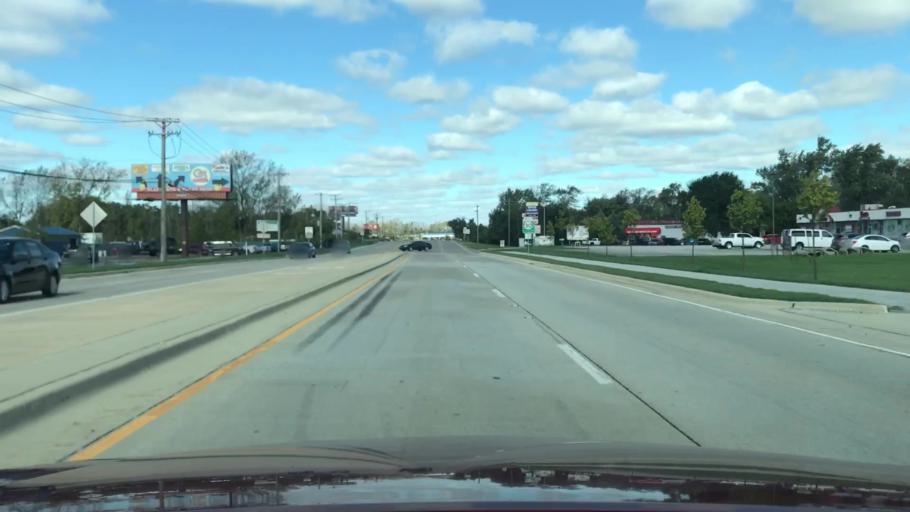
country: US
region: Indiana
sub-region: Lake County
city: Dyer
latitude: 41.5021
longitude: -87.5299
